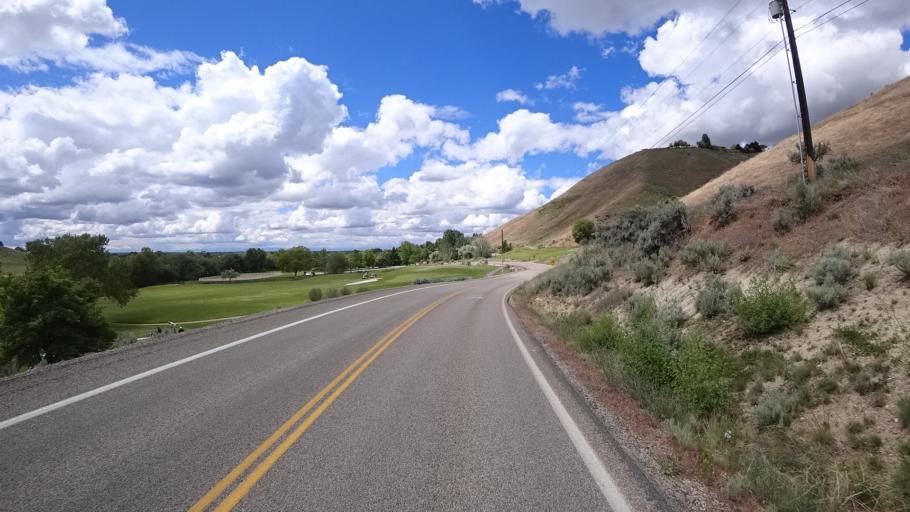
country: US
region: Idaho
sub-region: Ada County
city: Garden City
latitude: 43.6607
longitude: -116.2284
